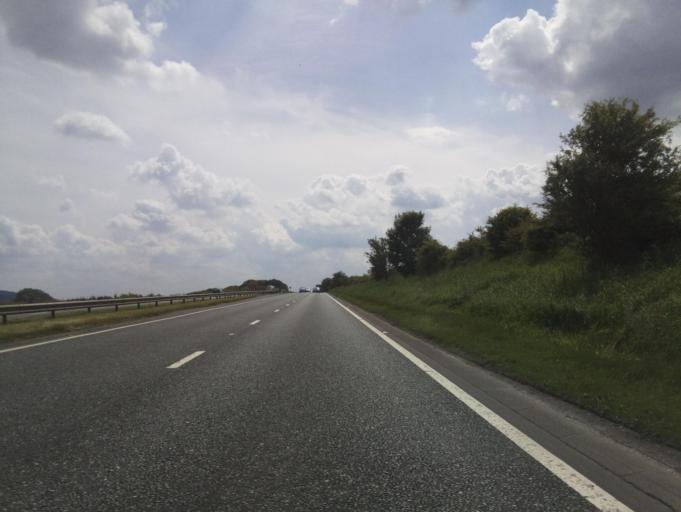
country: GB
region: England
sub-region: North Yorkshire
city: Thirsk
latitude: 54.3181
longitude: -1.3387
